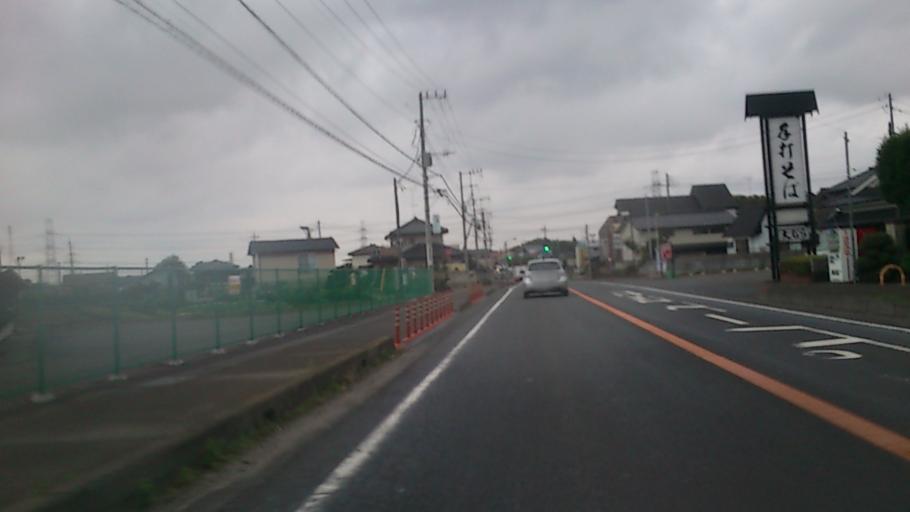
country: JP
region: Ibaraki
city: Sakai
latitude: 36.0975
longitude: 139.8210
